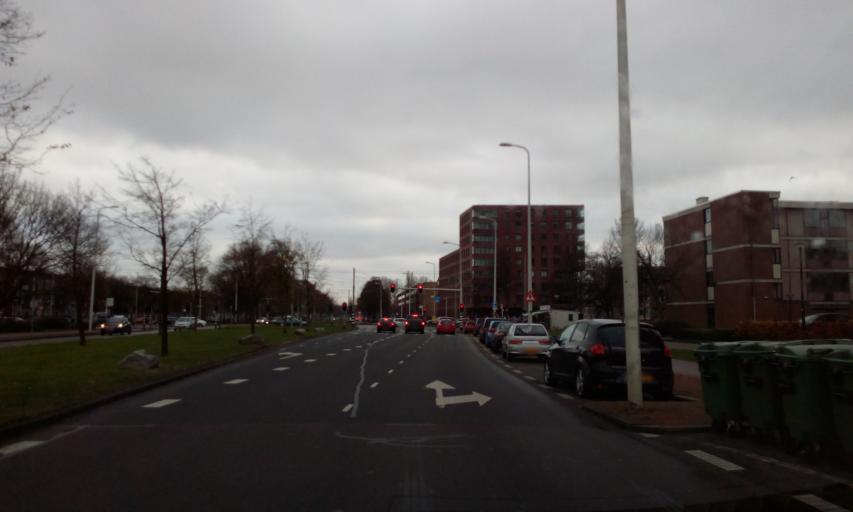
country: NL
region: South Holland
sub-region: Gemeente Den Haag
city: The Hague
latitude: 52.0495
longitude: 4.2830
